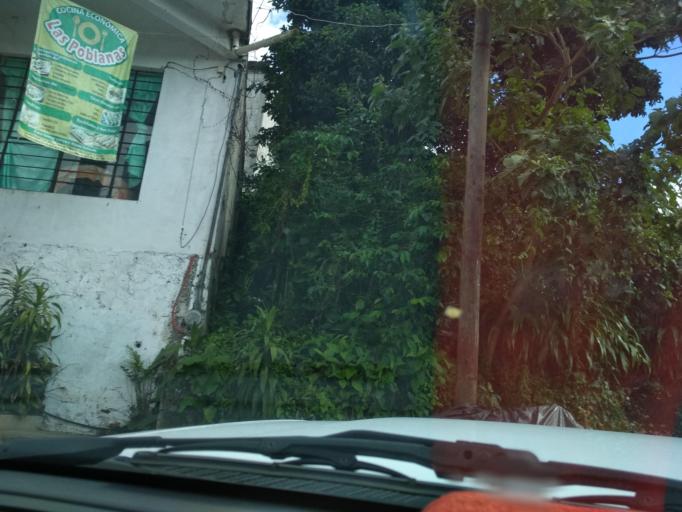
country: MX
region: Veracruz
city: Coatepec
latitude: 19.4546
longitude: -96.9361
